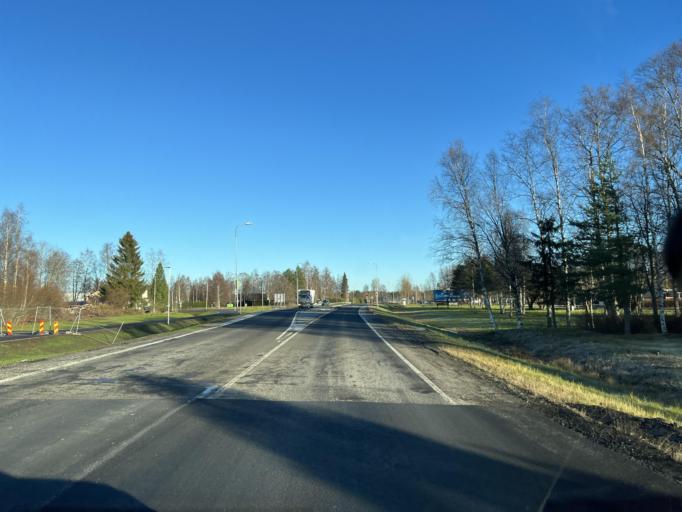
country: FI
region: Northern Ostrobothnia
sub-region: Ylivieska
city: Ylivieska
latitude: 64.0757
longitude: 24.5163
